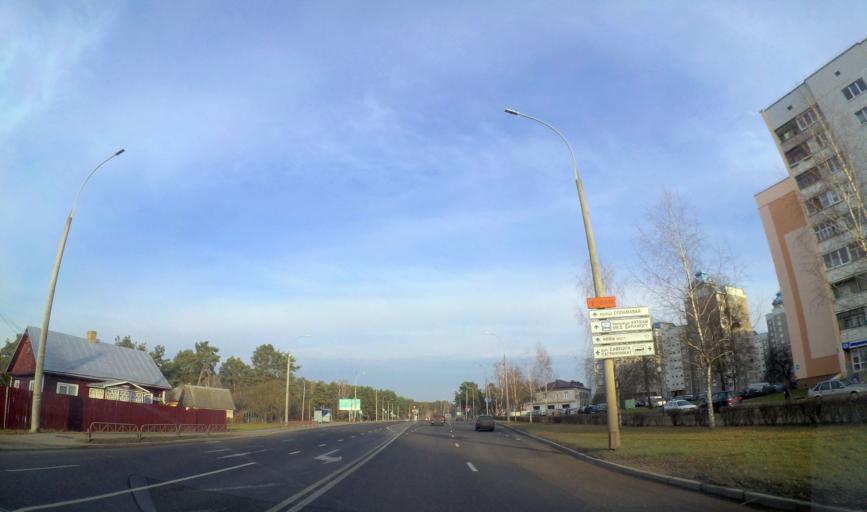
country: BY
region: Grodnenskaya
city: Hrodna
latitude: 53.6717
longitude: 23.7927
